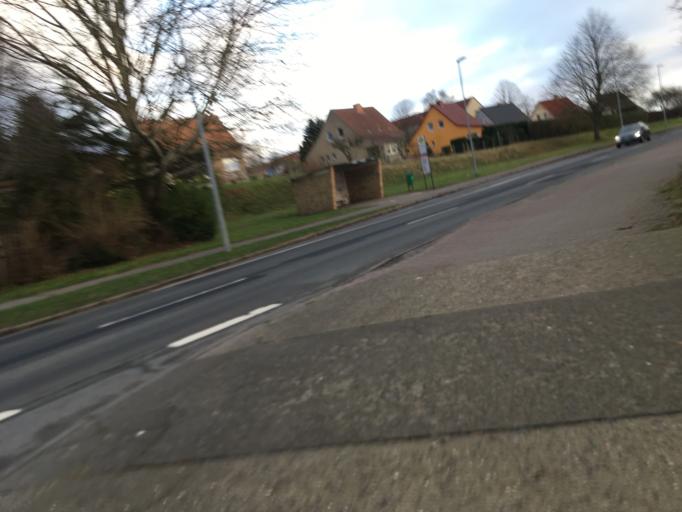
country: DE
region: Mecklenburg-Vorpommern
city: Sassnitz
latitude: 54.5121
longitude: 13.6228
